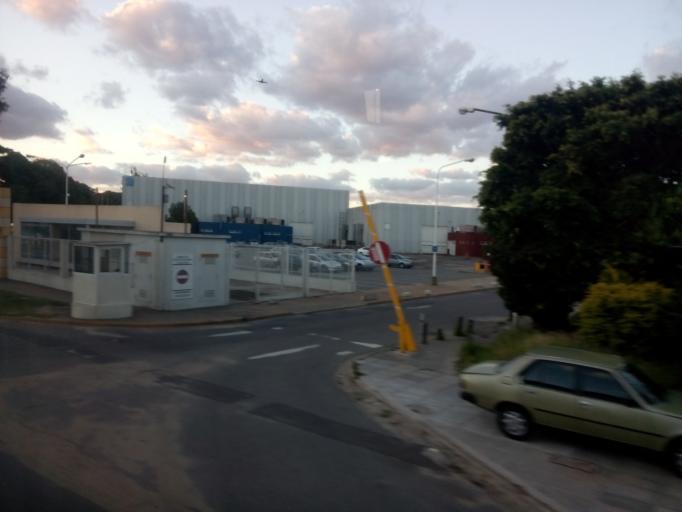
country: AR
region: Buenos Aires F.D.
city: Retiro
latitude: -34.5722
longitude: -58.3943
